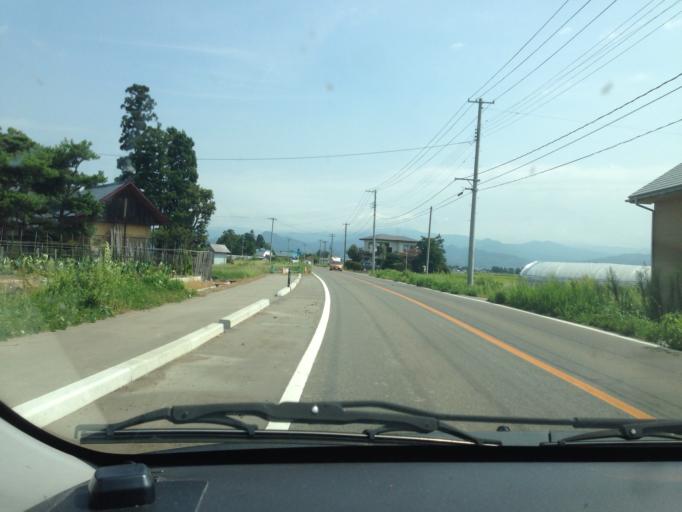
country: JP
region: Fukushima
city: Kitakata
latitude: 37.6152
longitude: 139.8596
